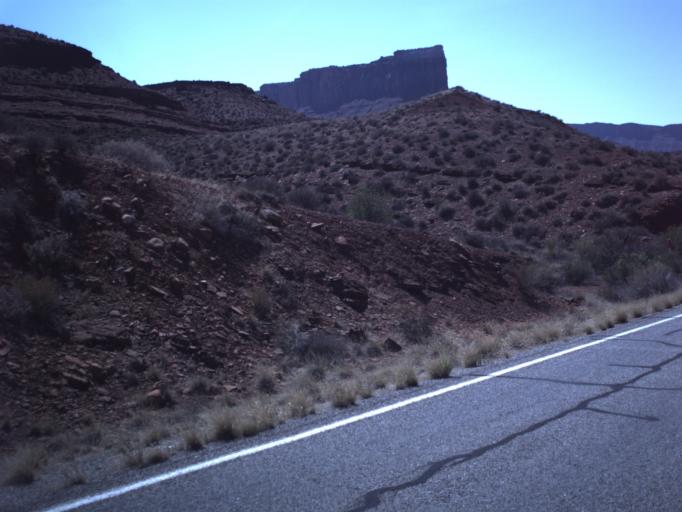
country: US
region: Utah
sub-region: Grand County
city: Moab
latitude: 38.7027
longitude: -109.3909
